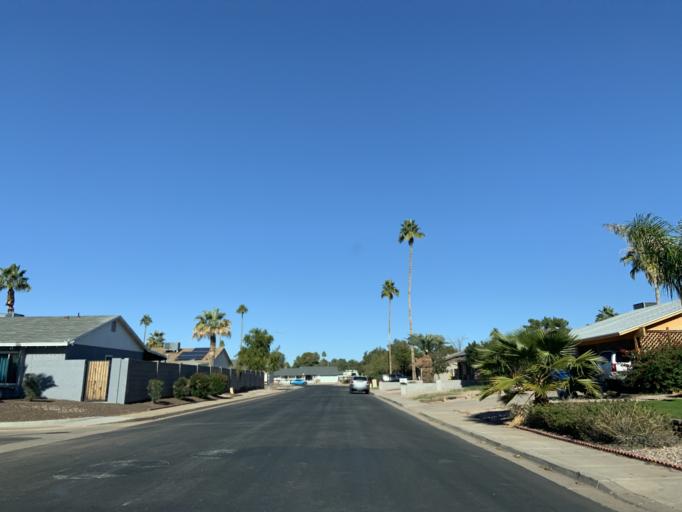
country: US
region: Arizona
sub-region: Maricopa County
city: San Carlos
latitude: 33.3722
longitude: -111.8566
